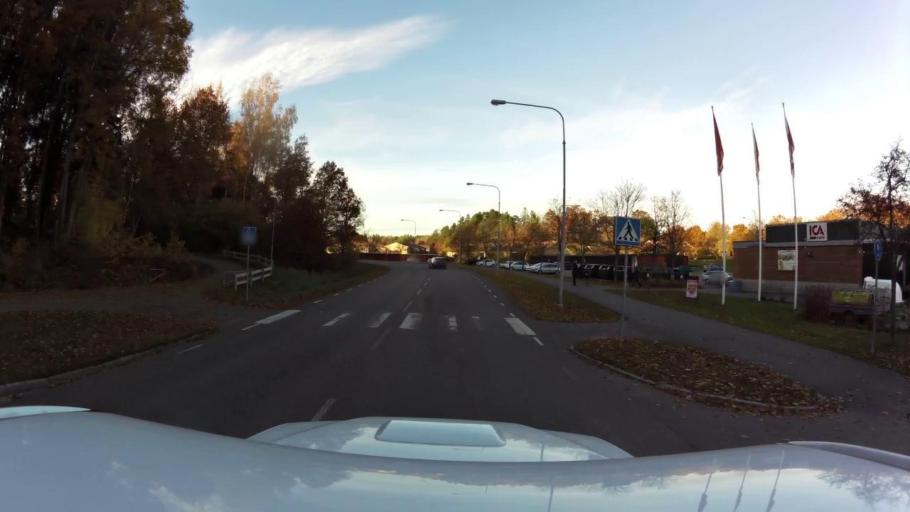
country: SE
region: OEstergoetland
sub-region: Linkopings Kommun
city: Sturefors
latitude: 58.3370
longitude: 15.7206
